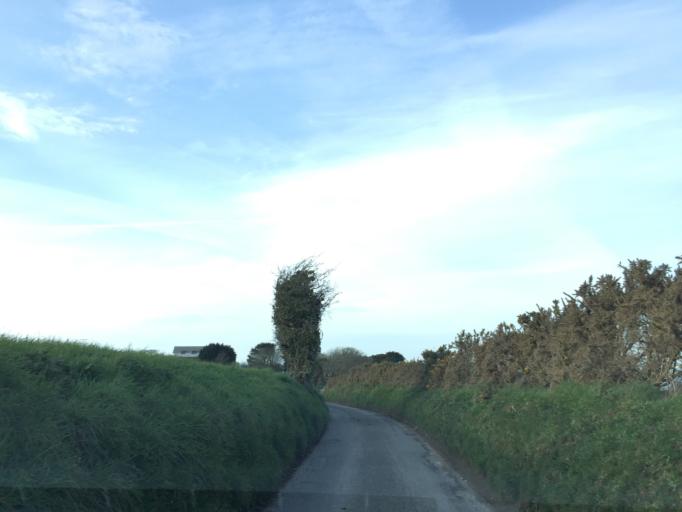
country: JE
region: St Helier
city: Saint Helier
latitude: 49.2458
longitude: -2.0983
